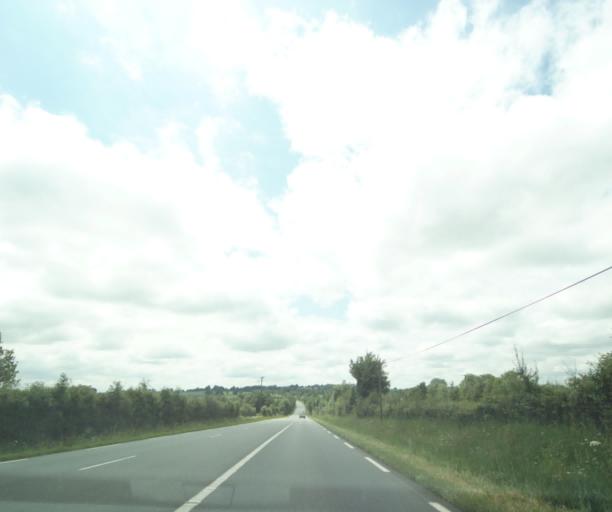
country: FR
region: Poitou-Charentes
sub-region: Departement des Deux-Sevres
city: Saint-Pardoux
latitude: 46.5930
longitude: -0.2906
